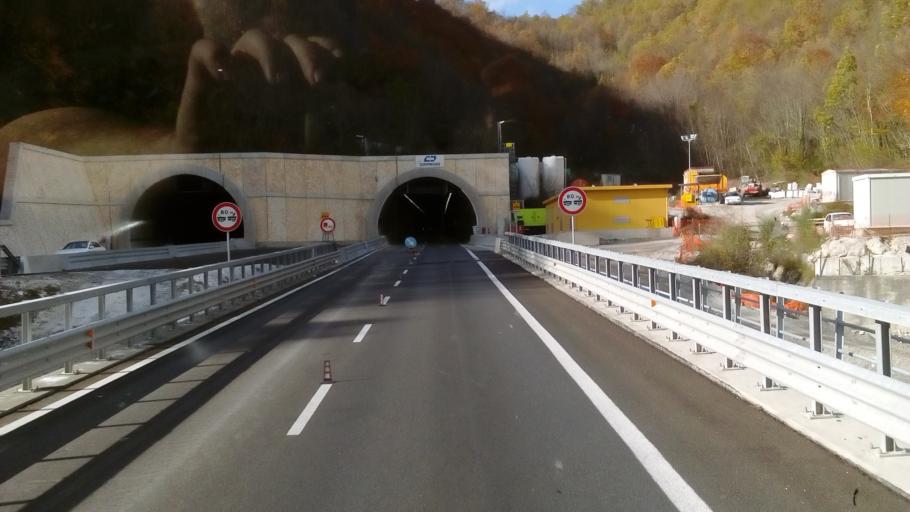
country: IT
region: Basilicate
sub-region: Provincia di Potenza
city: Castelluccio Superiore
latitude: 39.9923
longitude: 15.9304
